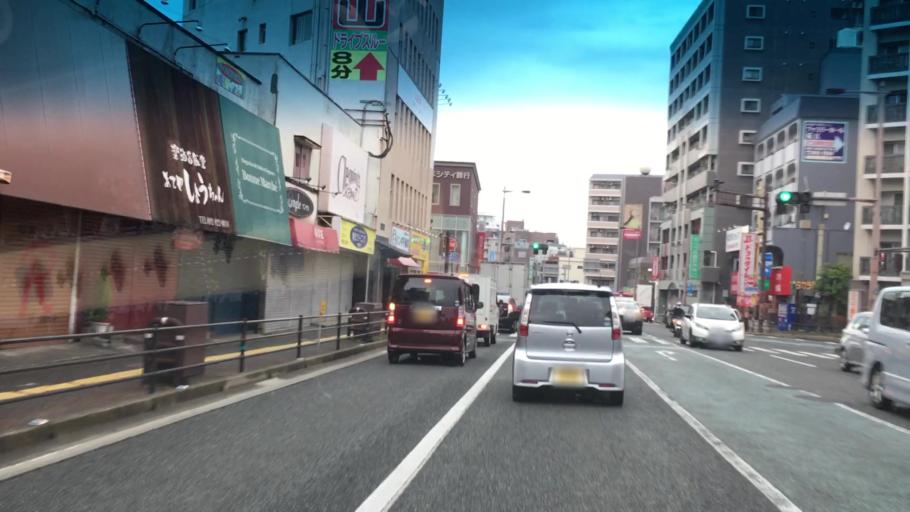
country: JP
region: Fukuoka
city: Fukuoka-shi
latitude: 33.5705
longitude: 130.3572
